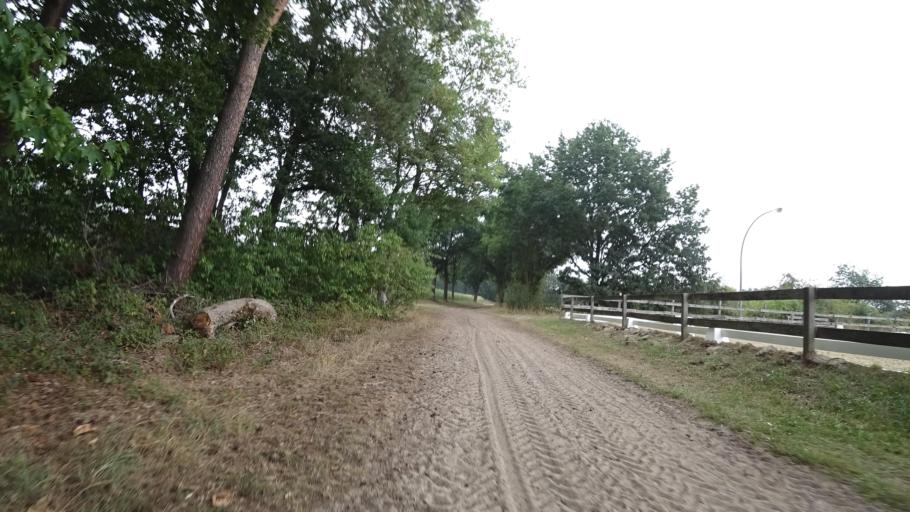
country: DE
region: North Rhine-Westphalia
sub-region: Regierungsbezirk Detmold
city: Guetersloh
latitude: 51.9107
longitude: 8.3219
